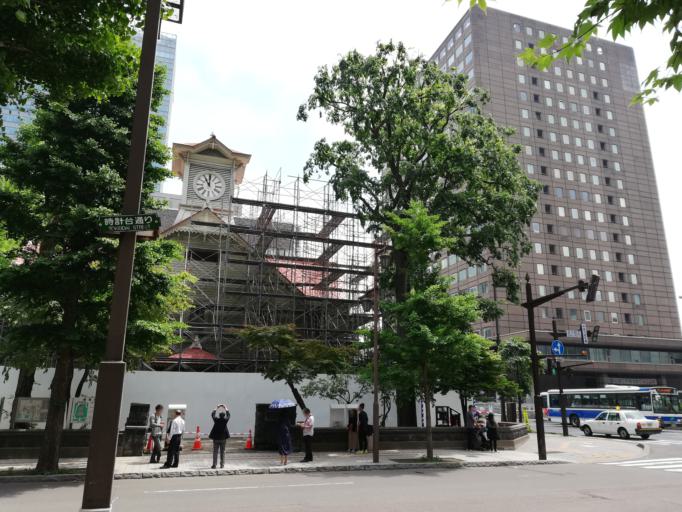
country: JP
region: Hokkaido
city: Sapporo
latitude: 43.0626
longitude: 141.3532
